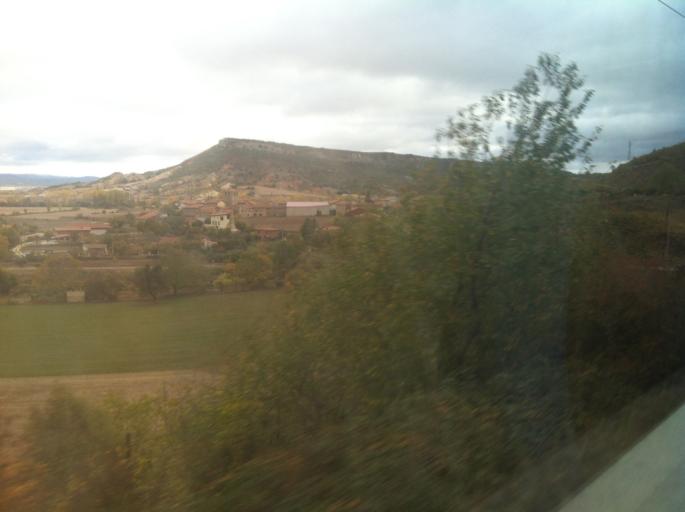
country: ES
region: Castille and Leon
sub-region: Provincia de Burgos
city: Bugedo
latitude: 42.6471
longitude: -3.0219
